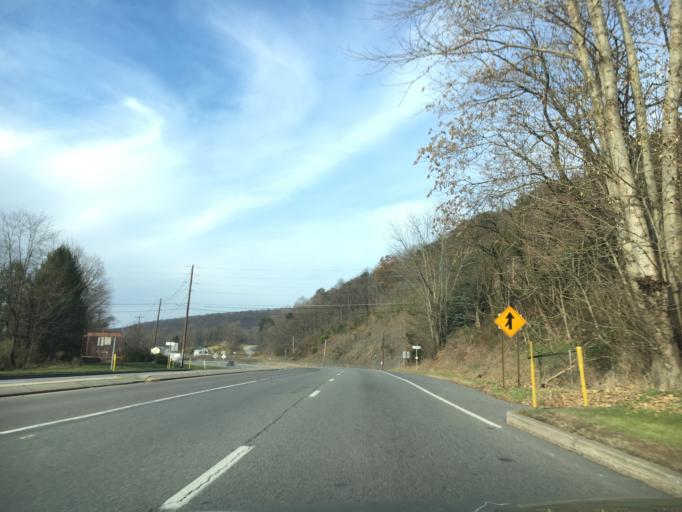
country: US
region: Pennsylvania
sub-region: Montour County
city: Danville
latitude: 40.9705
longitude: -76.6164
